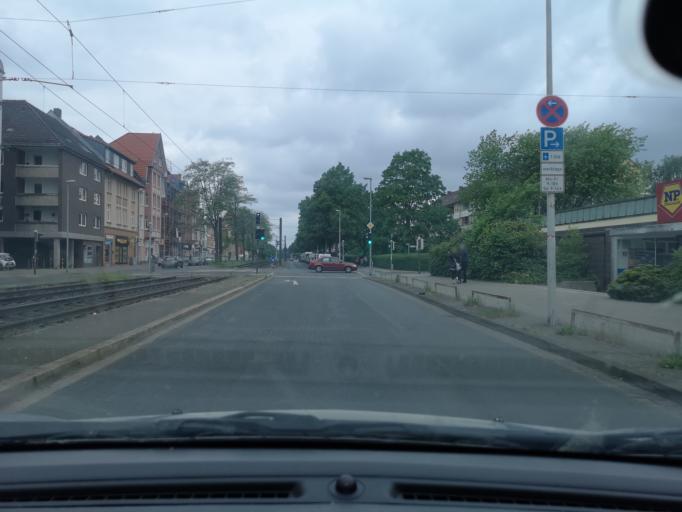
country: DE
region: Lower Saxony
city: Hannover
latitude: 52.3981
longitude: 9.6734
